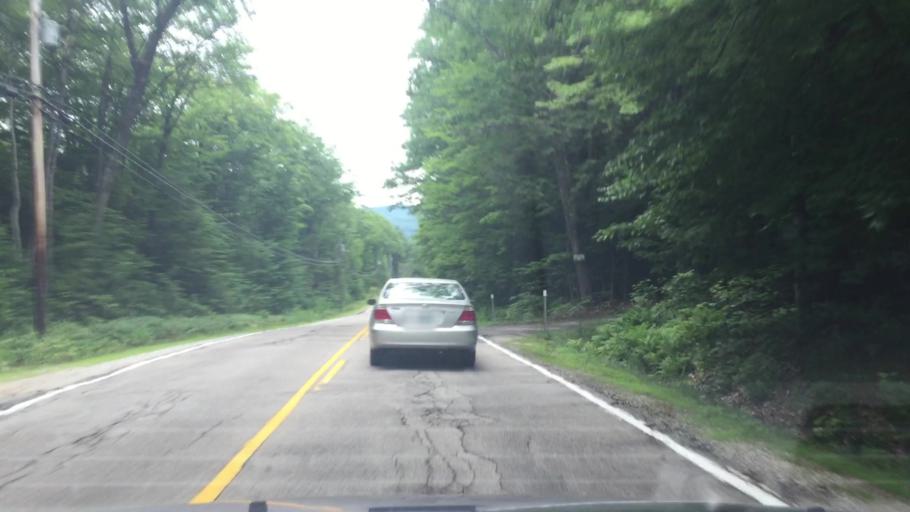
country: US
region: New Hampshire
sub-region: Carroll County
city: Conway
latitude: 43.9315
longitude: -71.0861
